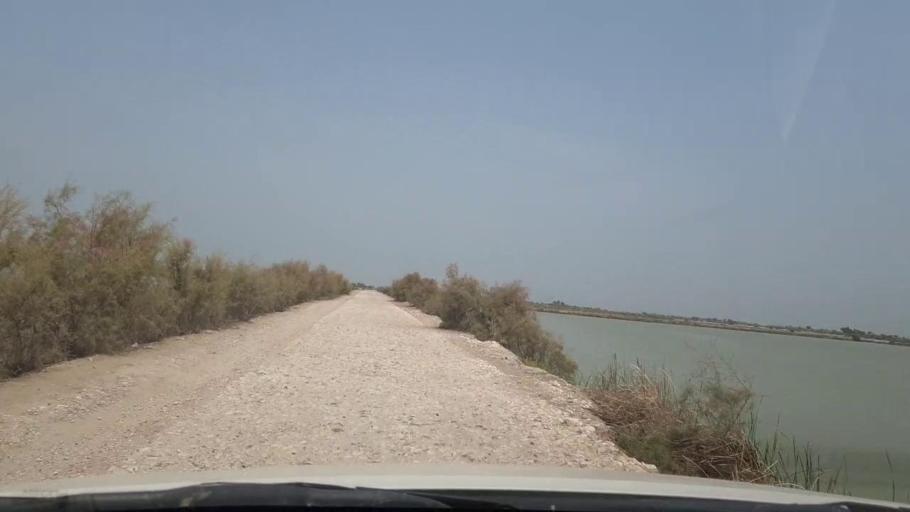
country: PK
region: Sindh
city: Rustam jo Goth
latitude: 28.0645
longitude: 68.8169
